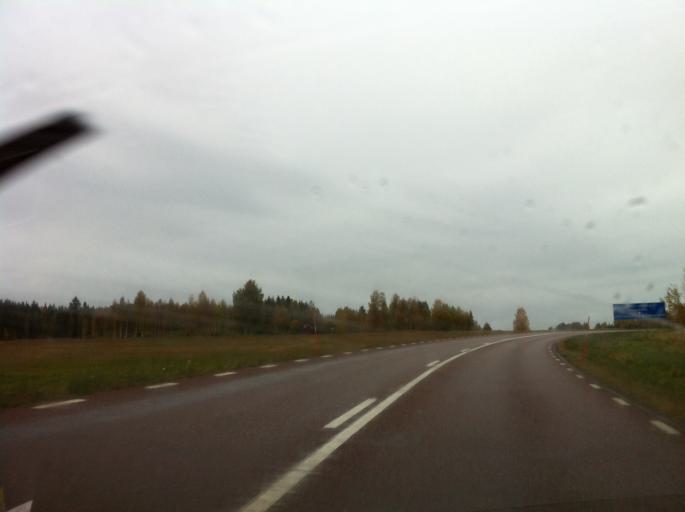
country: SE
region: Dalarna
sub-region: Ludvika Kommun
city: Grangesberg
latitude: 60.2170
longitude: 14.9570
